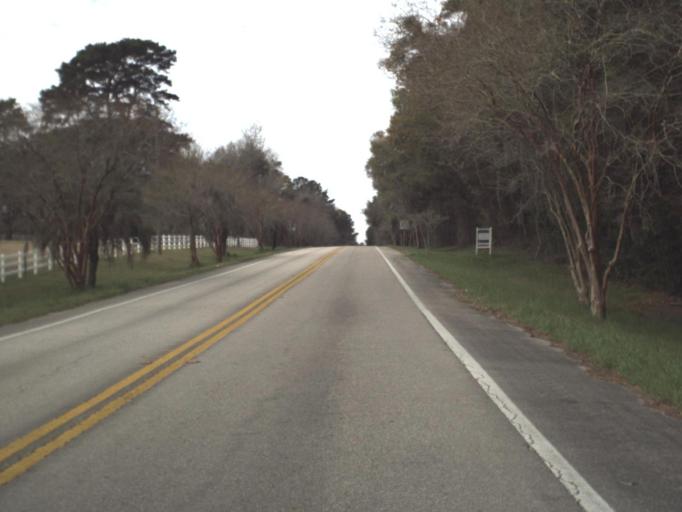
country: US
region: Florida
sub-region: Jefferson County
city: Monticello
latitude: 30.5318
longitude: -83.9584
